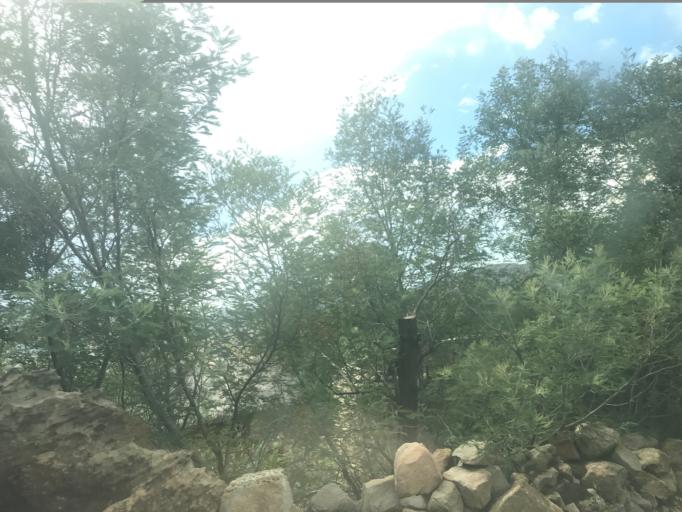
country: LS
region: Maseru
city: Nako
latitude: -29.6326
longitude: 27.5136
